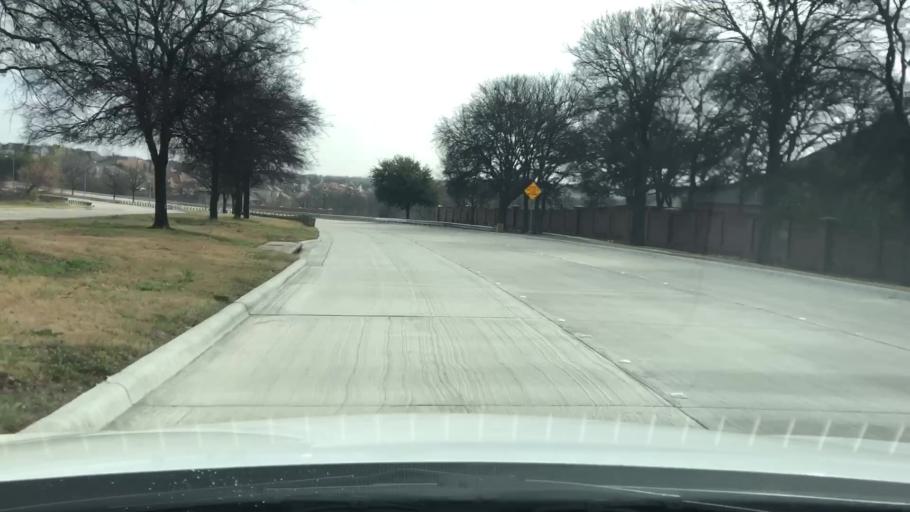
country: US
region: Texas
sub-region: Denton County
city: The Colony
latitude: 33.0713
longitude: -96.8507
